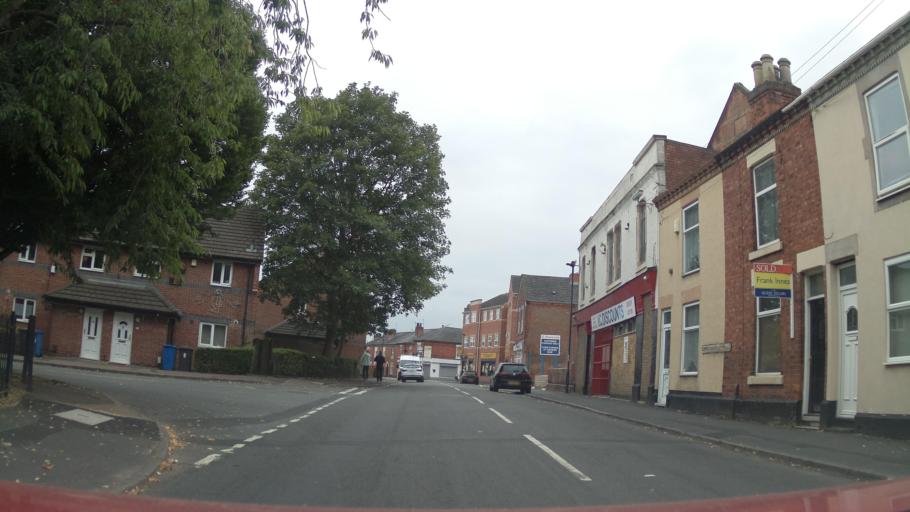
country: GB
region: England
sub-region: Derby
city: Derby
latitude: 52.9166
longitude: -1.4946
